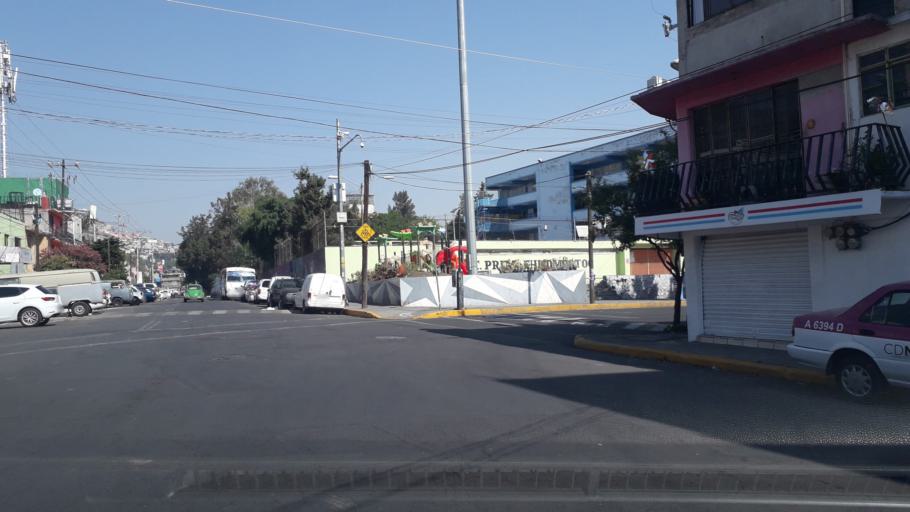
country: MX
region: Mexico City
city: Gustavo A. Madero
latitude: 19.5038
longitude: -99.0961
